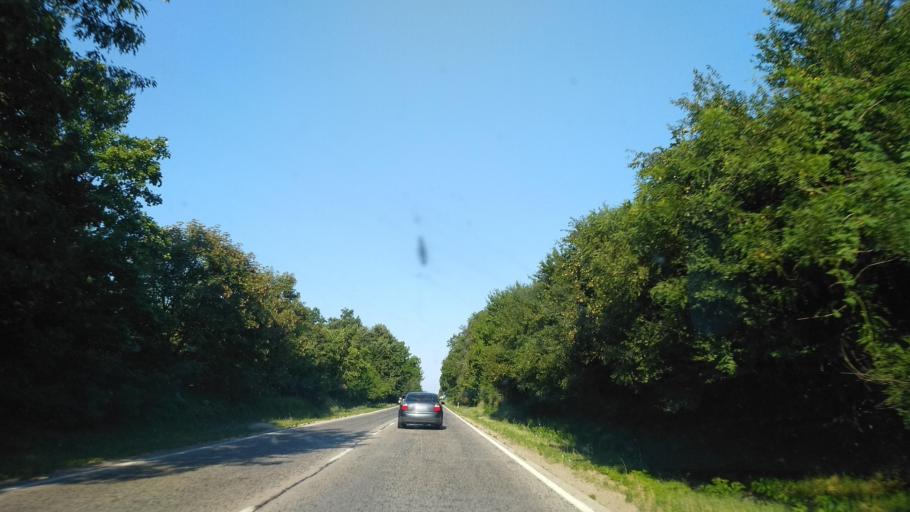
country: BG
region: Lovech
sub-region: Obshtina Lovech
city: Lovech
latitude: 43.0528
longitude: 24.8214
